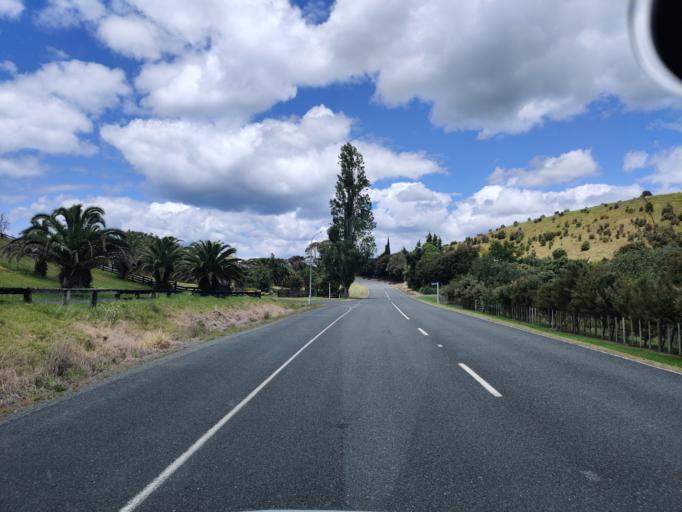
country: NZ
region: Northland
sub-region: Far North District
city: Paihia
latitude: -35.2775
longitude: 174.1399
